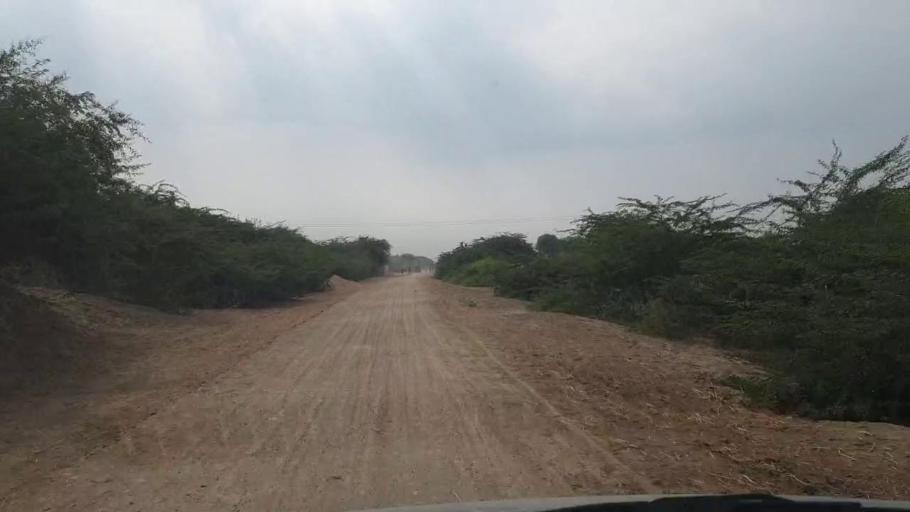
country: PK
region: Sindh
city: Talhar
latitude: 24.9374
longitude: 68.7892
